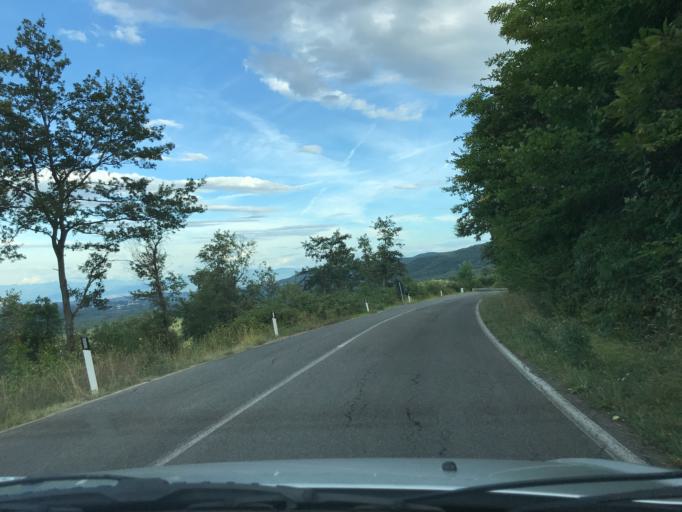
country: IT
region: Umbria
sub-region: Provincia di Terni
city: Guardea
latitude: 42.6520
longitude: 12.3520
